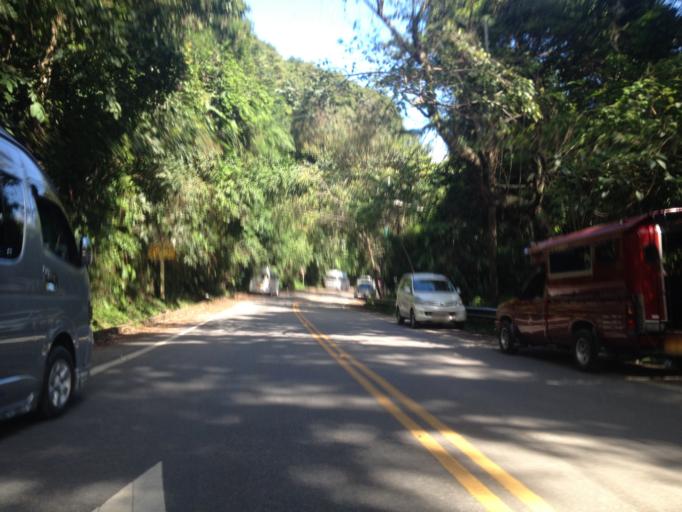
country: TH
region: Chiang Mai
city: Chiang Mai
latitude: 18.8047
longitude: 98.9170
